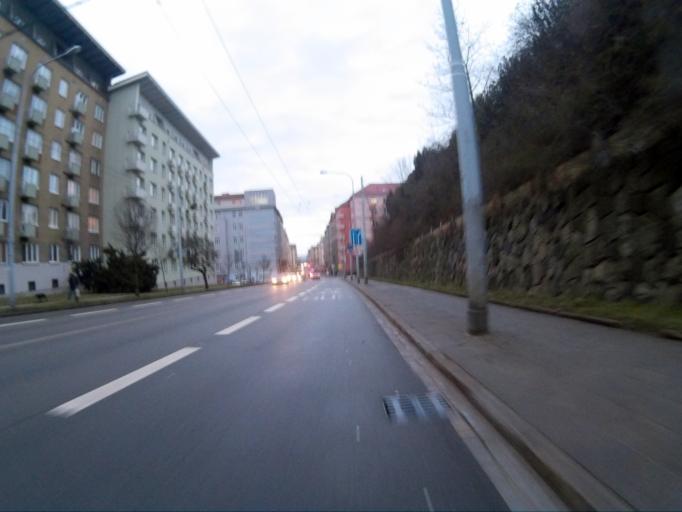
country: CZ
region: South Moravian
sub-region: Mesto Brno
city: Brno
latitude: 49.2015
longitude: 16.5927
